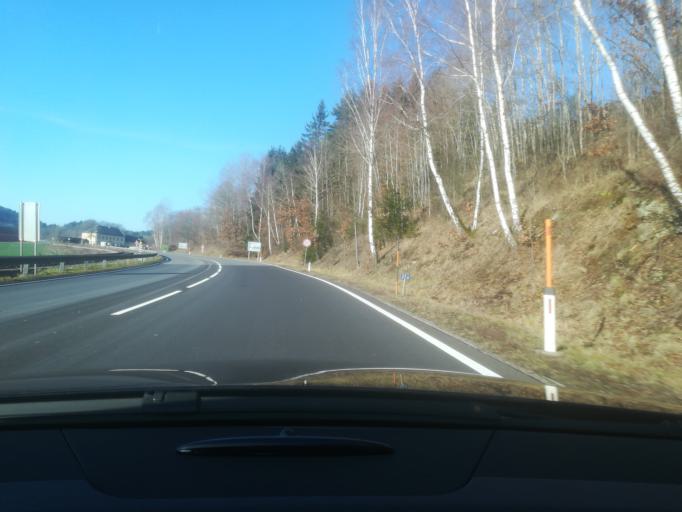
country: AT
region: Upper Austria
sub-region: Politischer Bezirk Urfahr-Umgebung
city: Herzogsdorf
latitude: 48.3948
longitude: 14.0816
